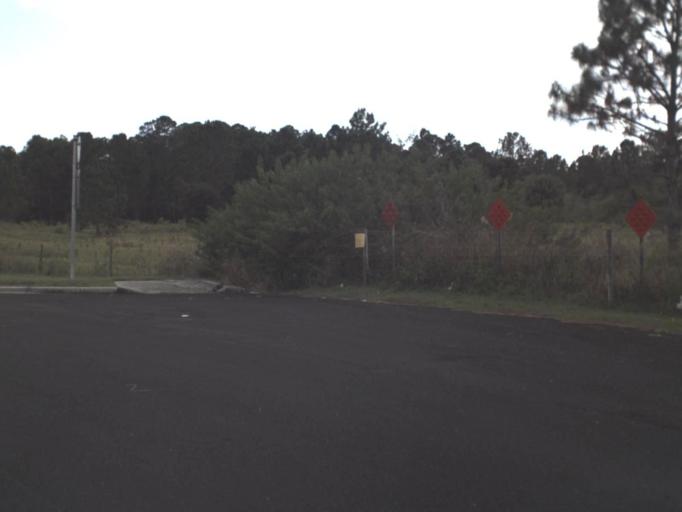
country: US
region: Florida
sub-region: Osceola County
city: Celebration
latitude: 28.3398
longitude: -81.5139
